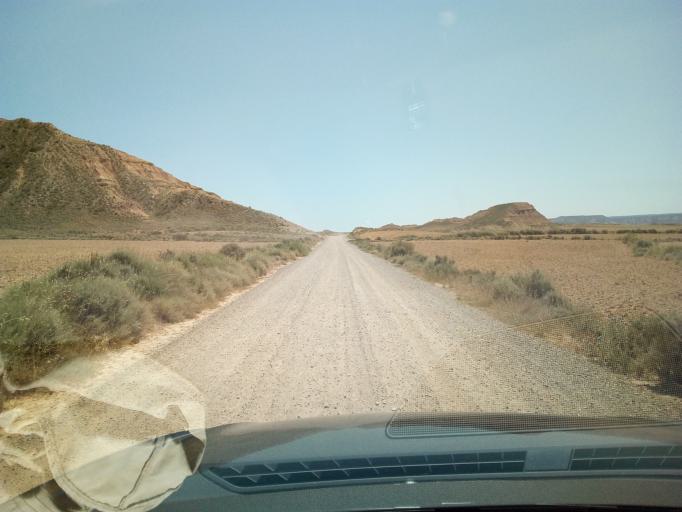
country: ES
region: Navarre
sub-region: Provincia de Navarra
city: Arguedas
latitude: 42.2085
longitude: -1.5124
